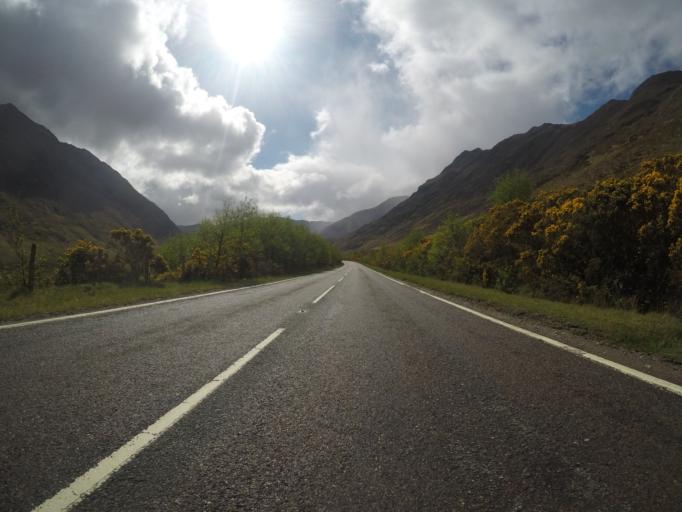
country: GB
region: Scotland
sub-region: Highland
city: Fort William
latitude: 57.1930
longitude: -5.3873
